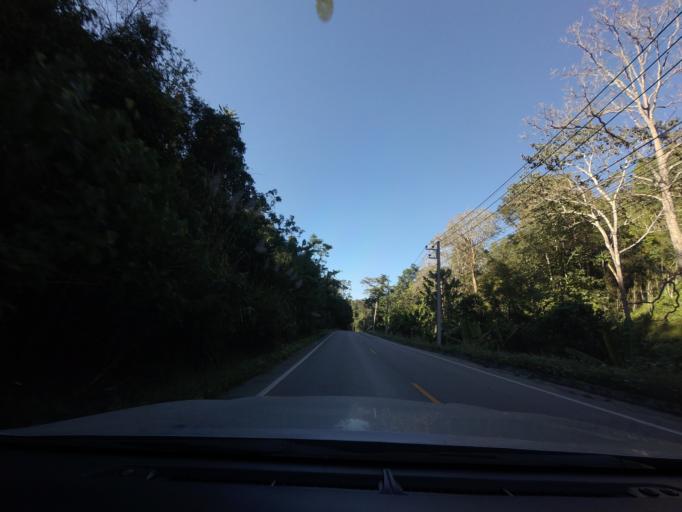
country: TH
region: Chiang Mai
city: Mae Taeng
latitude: 19.1904
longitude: 98.6909
